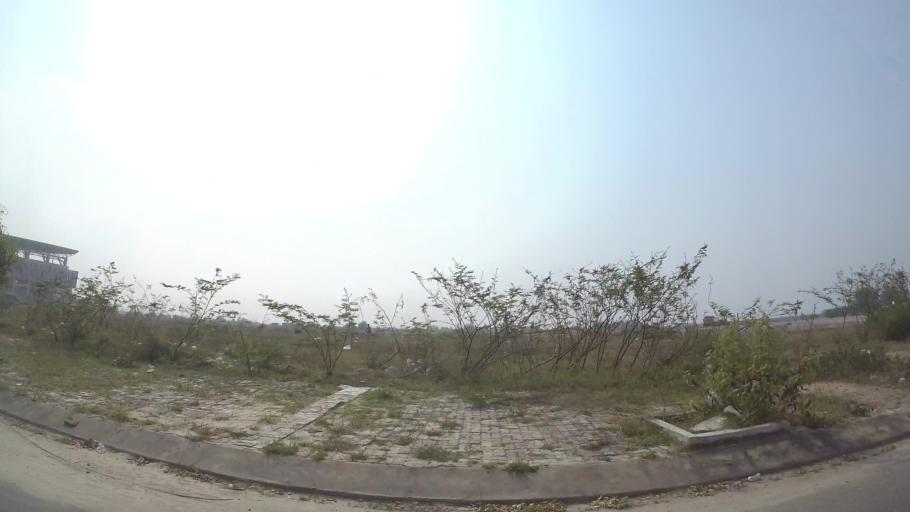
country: VN
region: Da Nang
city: Cam Le
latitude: 15.9988
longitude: 108.2204
